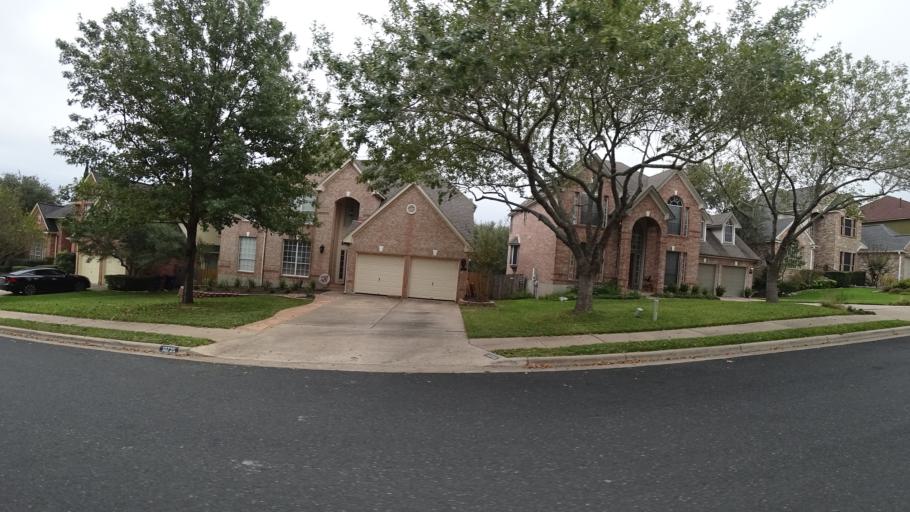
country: US
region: Texas
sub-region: Williamson County
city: Anderson Mill
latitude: 30.4371
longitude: -97.8194
